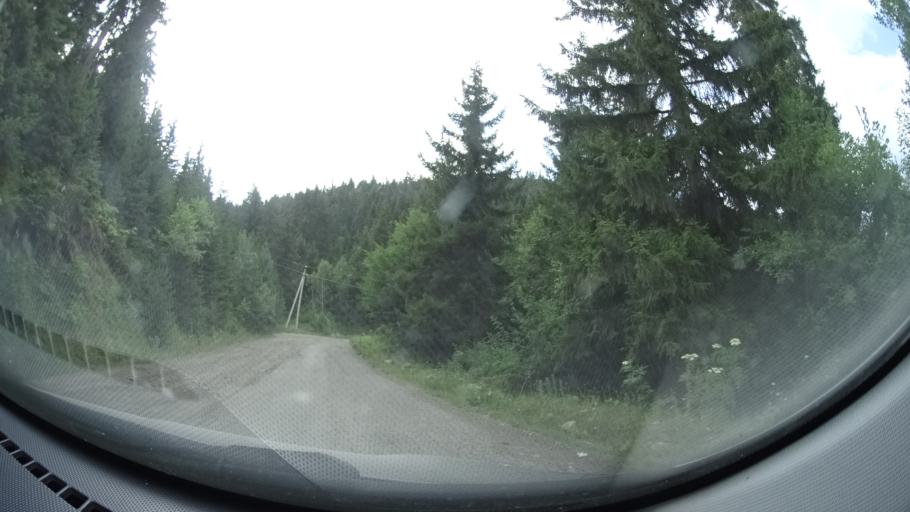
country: GE
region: Samtskhe-Javakheti
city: Adigeni
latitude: 41.6647
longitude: 42.6136
